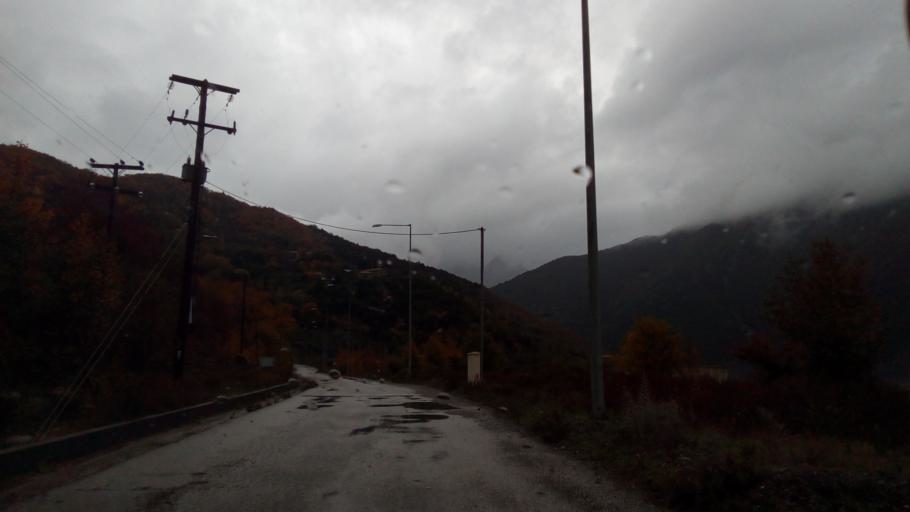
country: GR
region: West Greece
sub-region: Nomos Aitolias kai Akarnanias
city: Thermo
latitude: 38.6610
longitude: 21.8446
